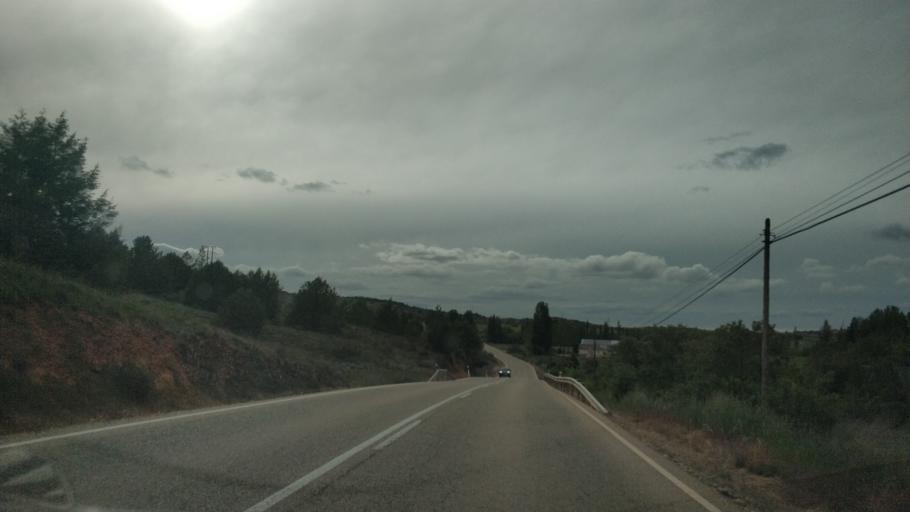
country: ES
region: Castille and Leon
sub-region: Provincia de Soria
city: El Burgo de Osma
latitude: 41.5781
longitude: -3.0324
